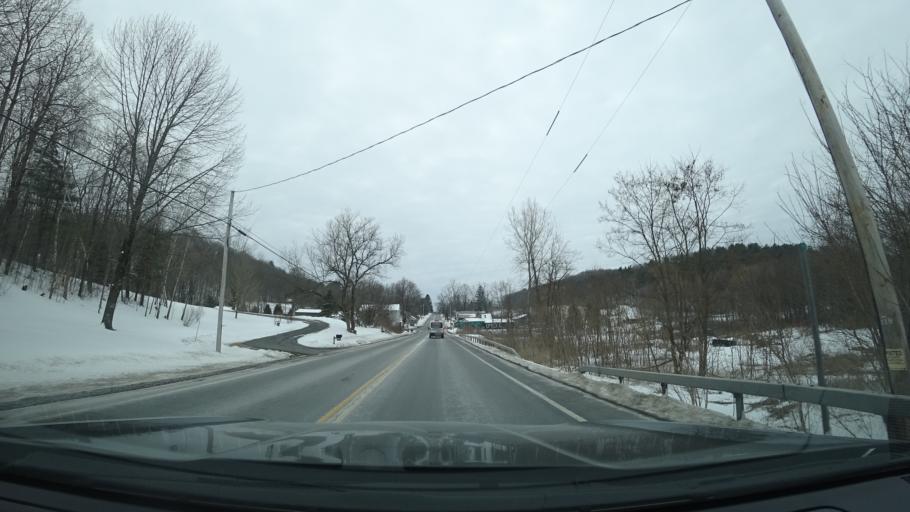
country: US
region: New York
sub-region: Washington County
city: Greenwich
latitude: 43.1861
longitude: -73.4927
